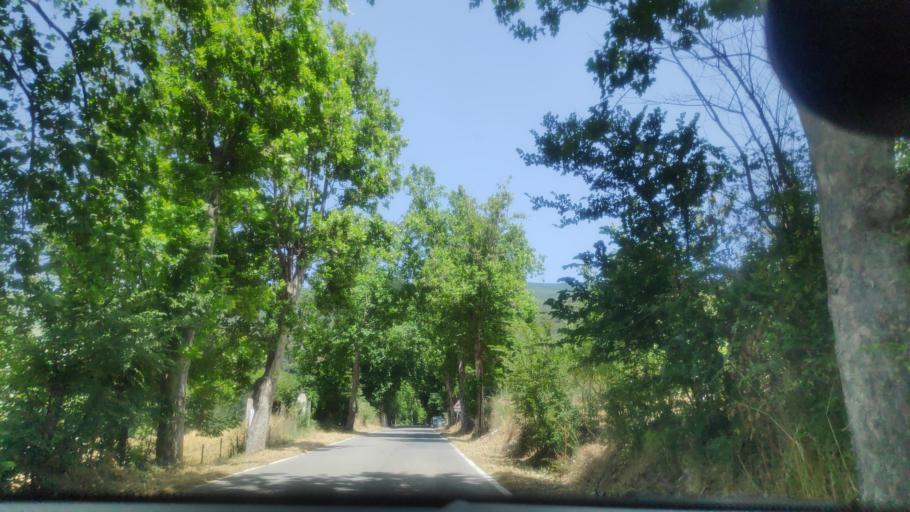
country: ES
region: Andalusia
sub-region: Provincia de Granada
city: Portugos
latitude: 36.9382
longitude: -3.3030
